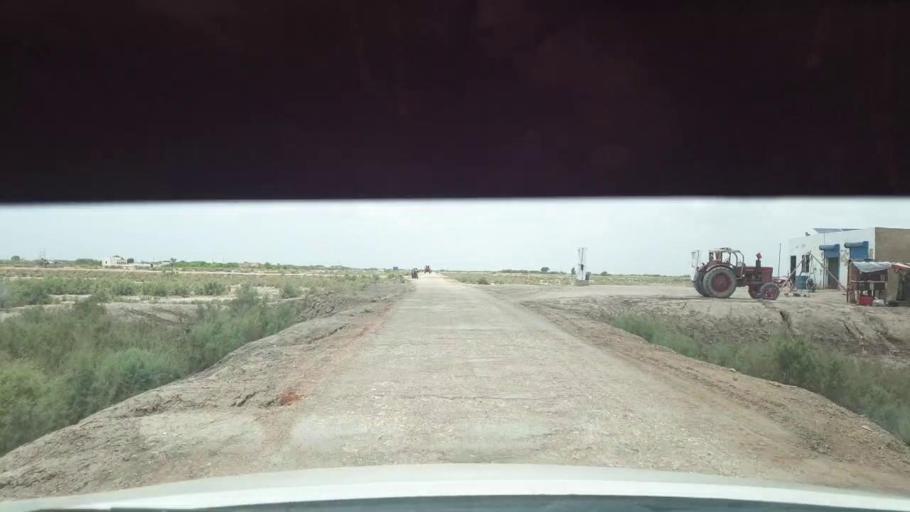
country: PK
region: Sindh
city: Kadhan
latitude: 24.5484
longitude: 69.1245
